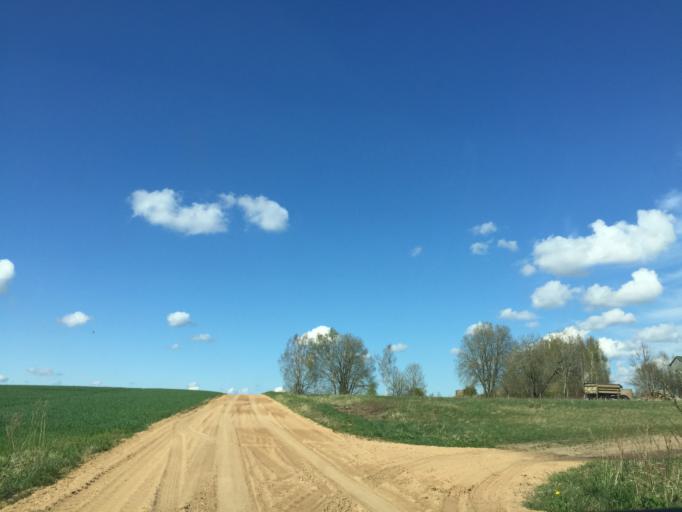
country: LV
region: Strenci
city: Strenci
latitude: 57.5369
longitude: 25.6908
